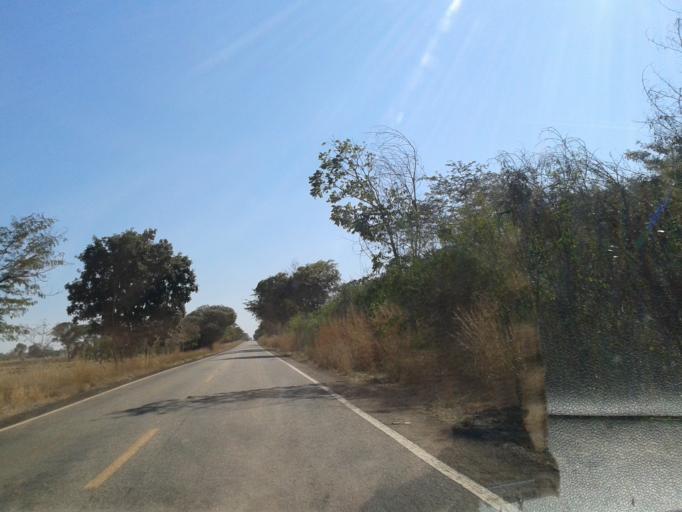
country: BR
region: Goias
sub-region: Mozarlandia
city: Mozarlandia
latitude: -14.2904
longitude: -50.4023
